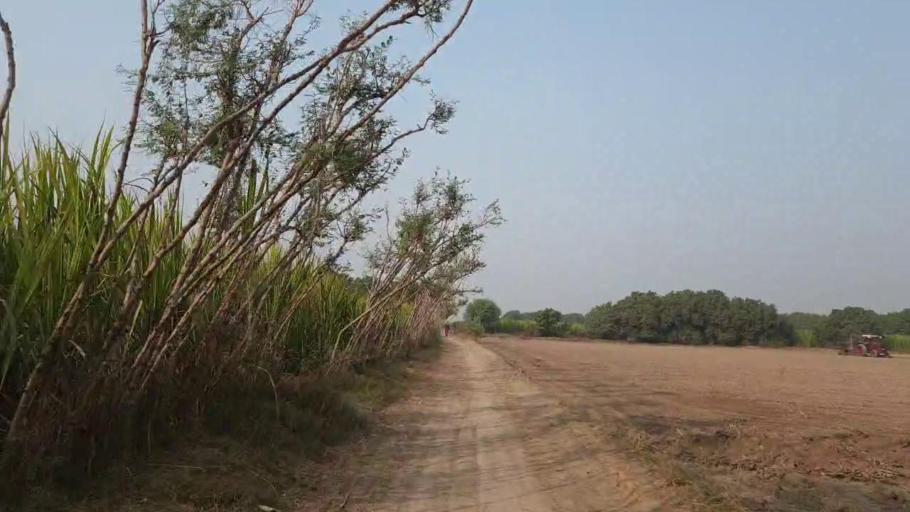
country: PK
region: Sindh
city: Tando Muhammad Khan
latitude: 25.1451
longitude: 68.6168
